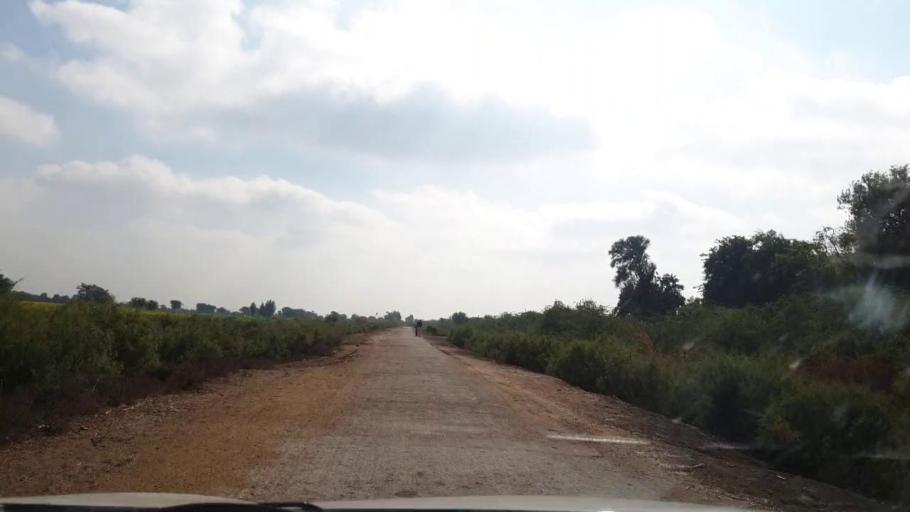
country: PK
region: Sindh
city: Berani
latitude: 25.7831
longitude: 68.9660
